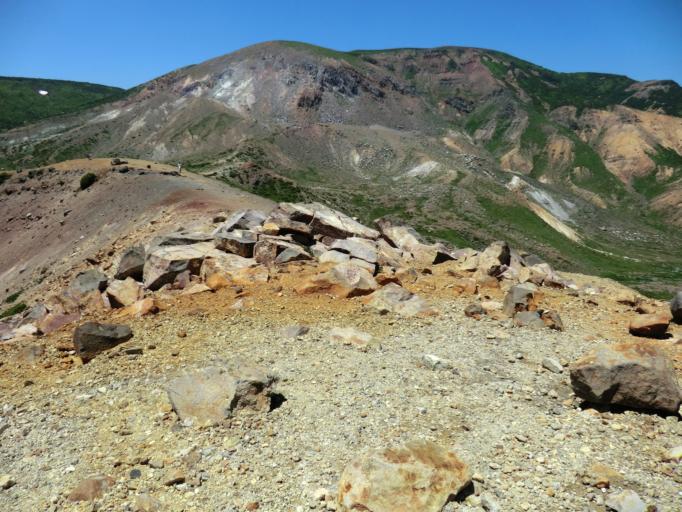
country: JP
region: Fukushima
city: Fukushima-shi
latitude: 37.7237
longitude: 140.2617
